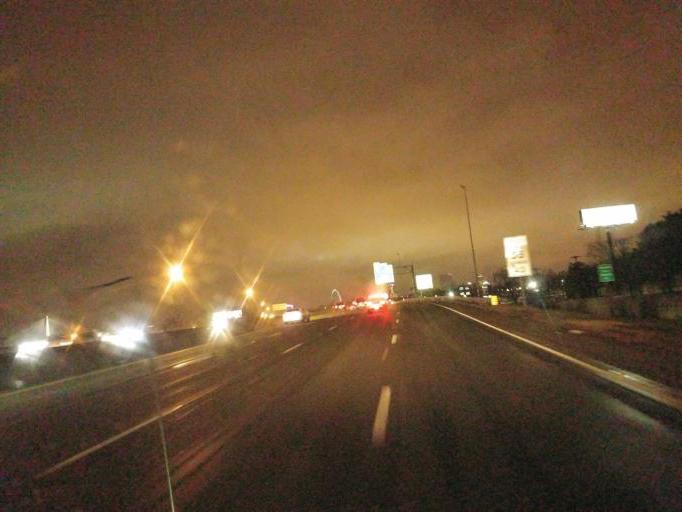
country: US
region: Illinois
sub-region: Madison County
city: Venice
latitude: 38.6584
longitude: -90.1965
